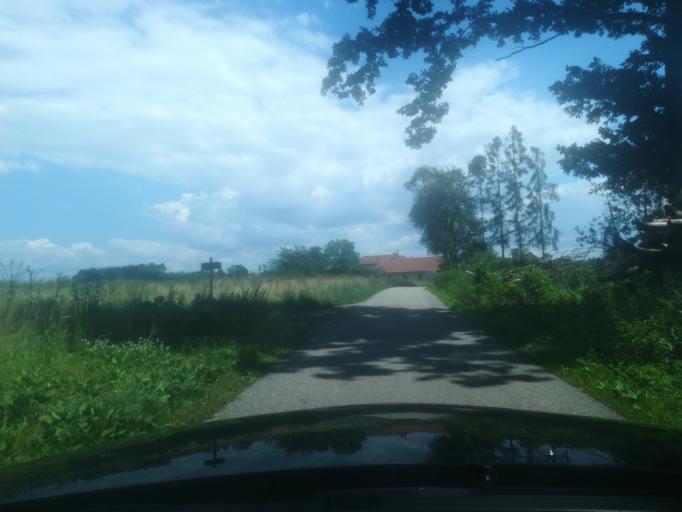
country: AT
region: Upper Austria
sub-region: Wels-Land
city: Holzhausen
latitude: 48.2413
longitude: 14.1234
